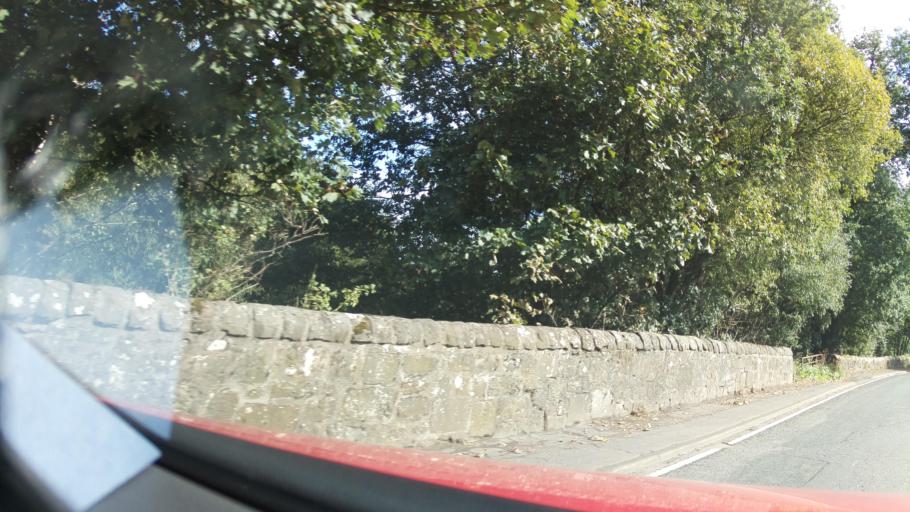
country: GB
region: Scotland
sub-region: Stirling
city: Cowie
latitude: 56.0373
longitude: -3.8569
